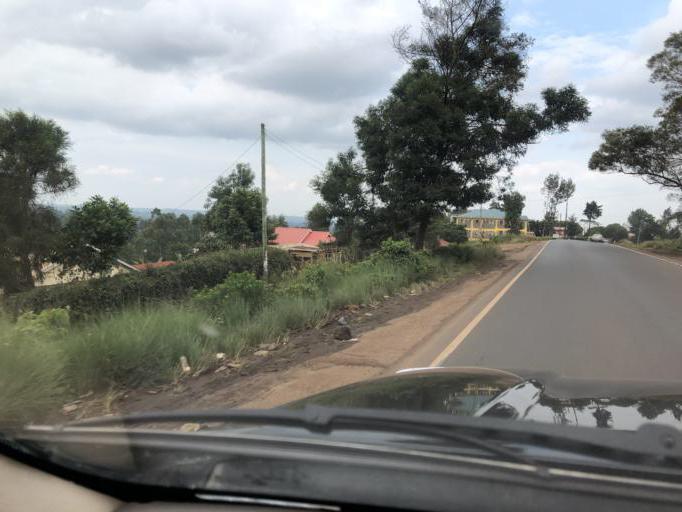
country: KE
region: Kiambu
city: Kikuyu
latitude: -1.2283
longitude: 36.6658
